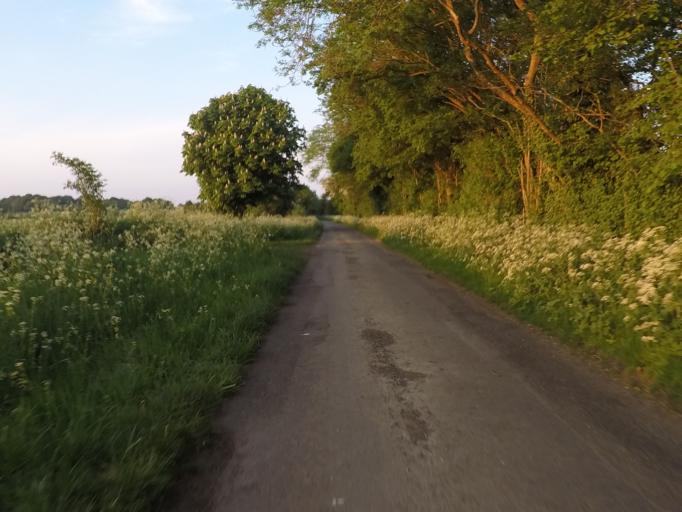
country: GB
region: England
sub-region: Oxfordshire
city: Witney
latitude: 51.8242
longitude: -1.4826
